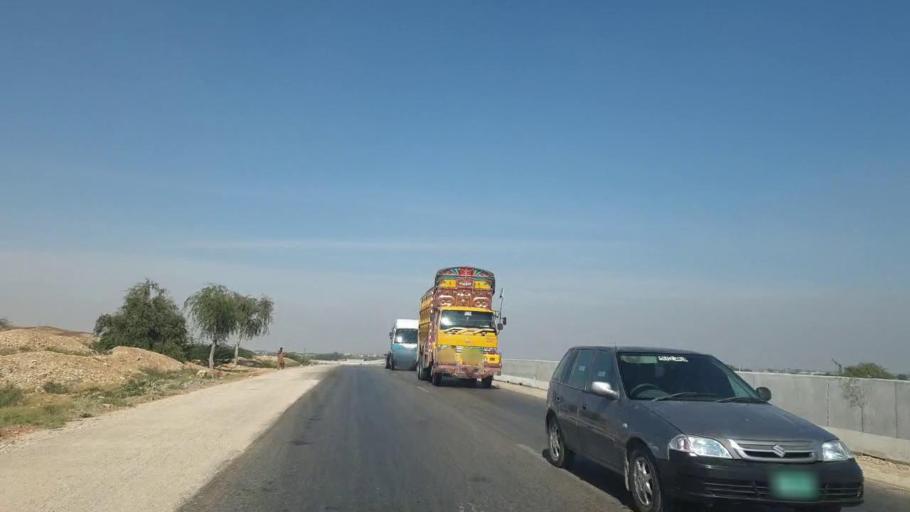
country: PK
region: Sindh
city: Matiari
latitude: 25.6799
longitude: 68.2962
